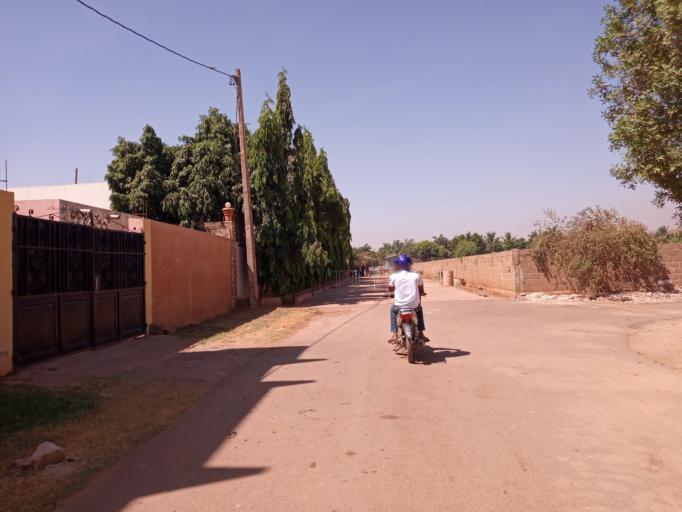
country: ML
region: Bamako
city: Bamako
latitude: 12.6026
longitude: -8.0477
